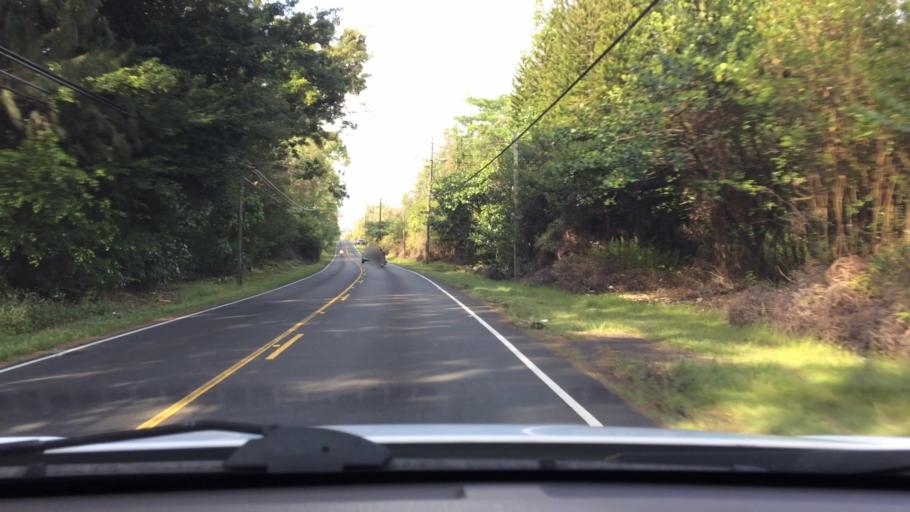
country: US
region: Hawaii
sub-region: Hawaii County
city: Hawaiian Paradise Park
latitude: 19.5055
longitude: -154.9510
